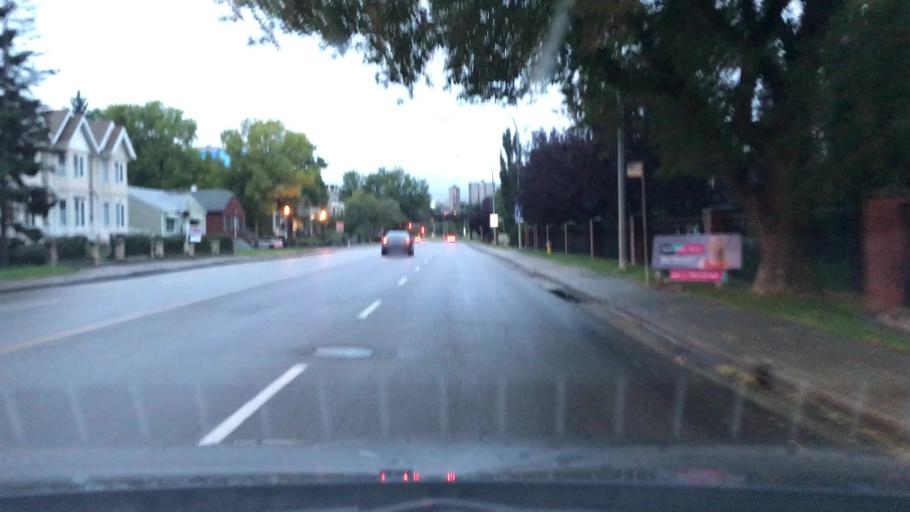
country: CA
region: Alberta
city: Edmonton
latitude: 53.5380
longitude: -113.4734
